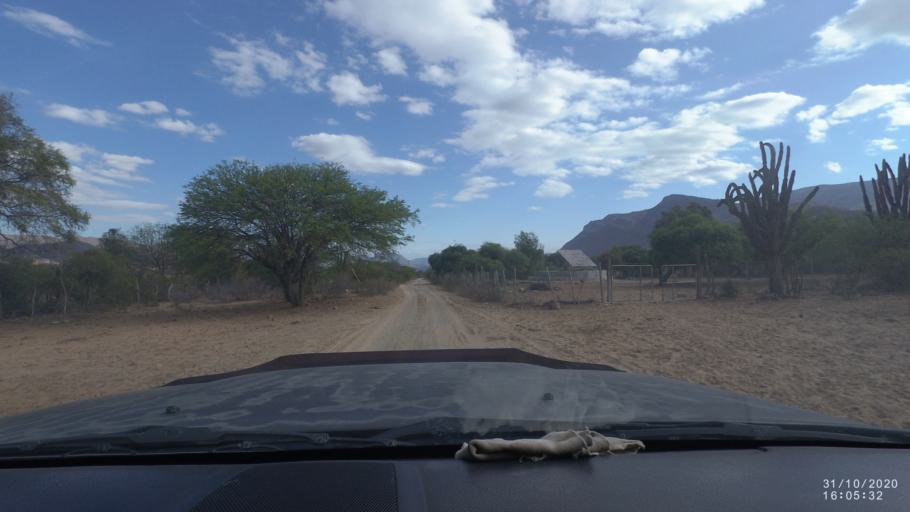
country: BO
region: Chuquisaca
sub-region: Provincia Zudanez
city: Mojocoya
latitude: -18.3671
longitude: -64.6494
